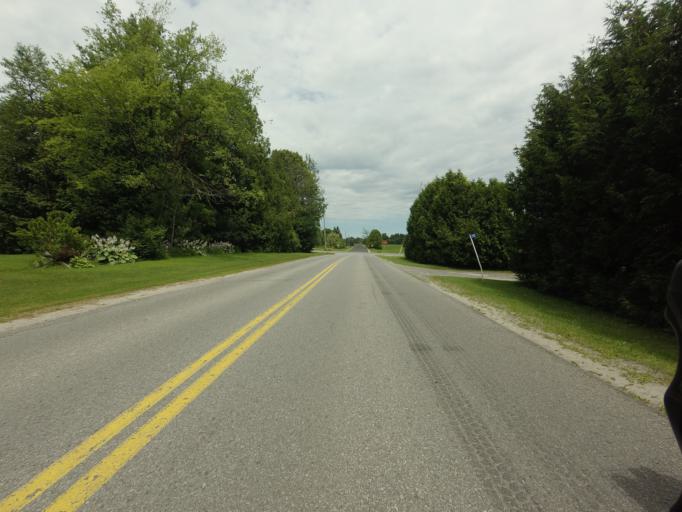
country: CA
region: Ontario
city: Bells Corners
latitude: 45.0587
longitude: -75.6101
